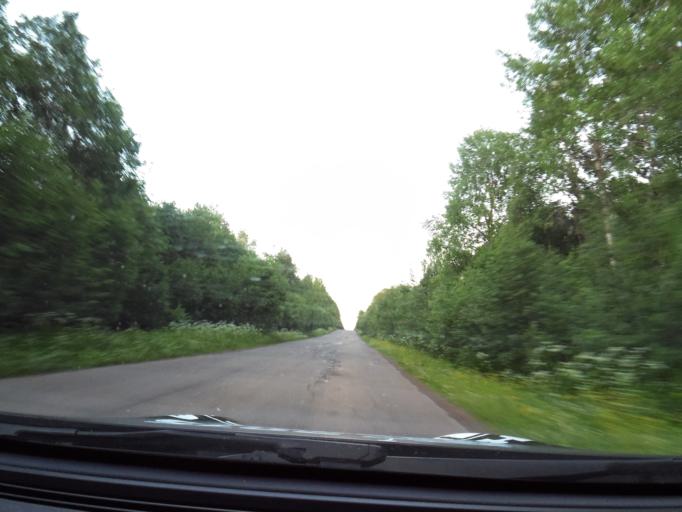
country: RU
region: Leningrad
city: Voznesen'ye
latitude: 60.8435
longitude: 35.6201
